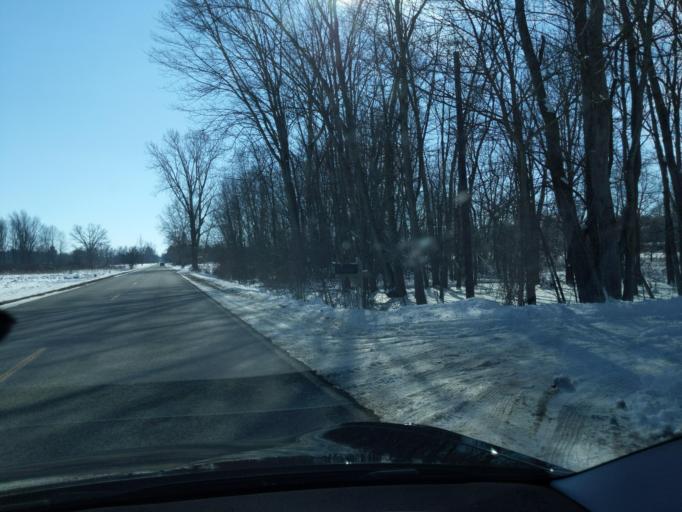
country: US
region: Michigan
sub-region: Livingston County
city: Fowlerville
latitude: 42.5955
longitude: -84.0748
